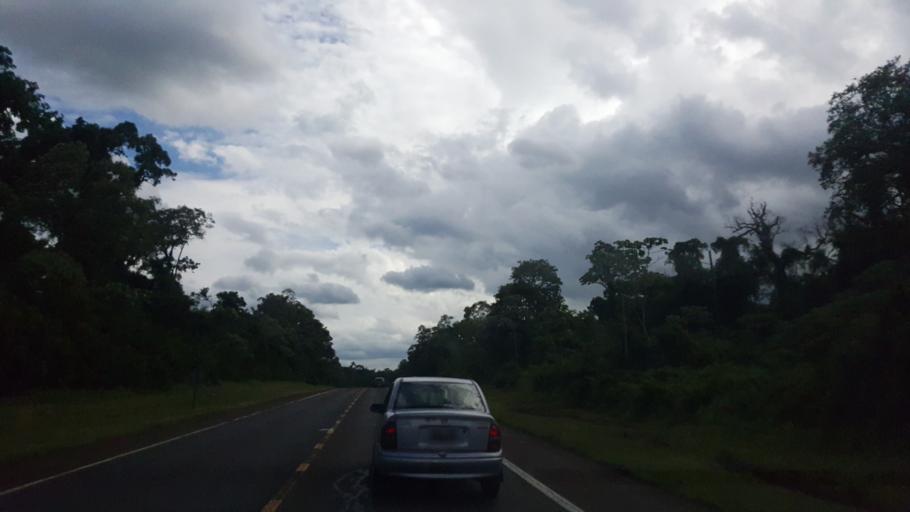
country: AR
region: Misiones
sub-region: Departamento de Iguazu
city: Puerto Iguazu
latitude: -25.7134
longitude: -54.5188
